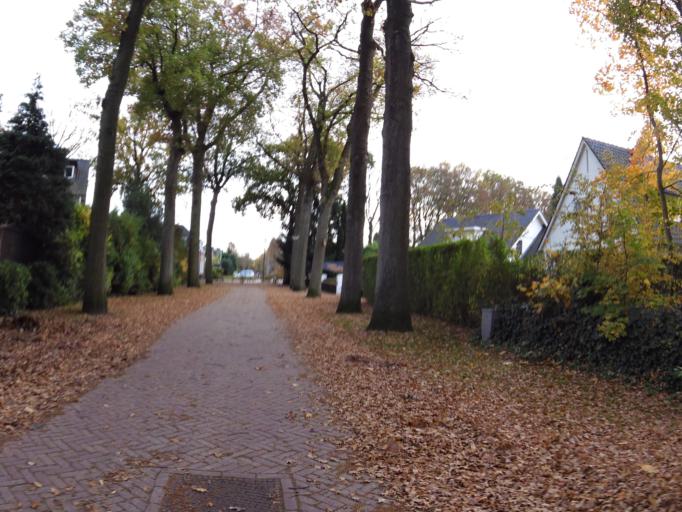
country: NL
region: North Brabant
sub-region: Gemeente Vught
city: Vught
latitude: 51.6660
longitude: 5.2862
